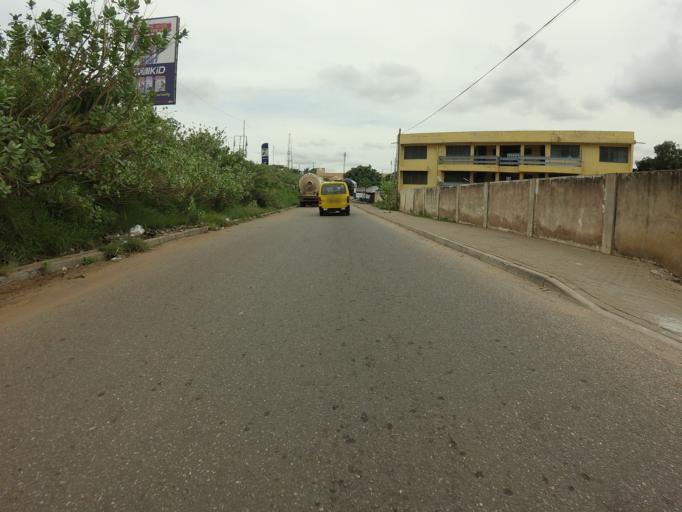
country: GH
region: Greater Accra
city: Accra
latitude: 5.5940
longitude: -0.2206
